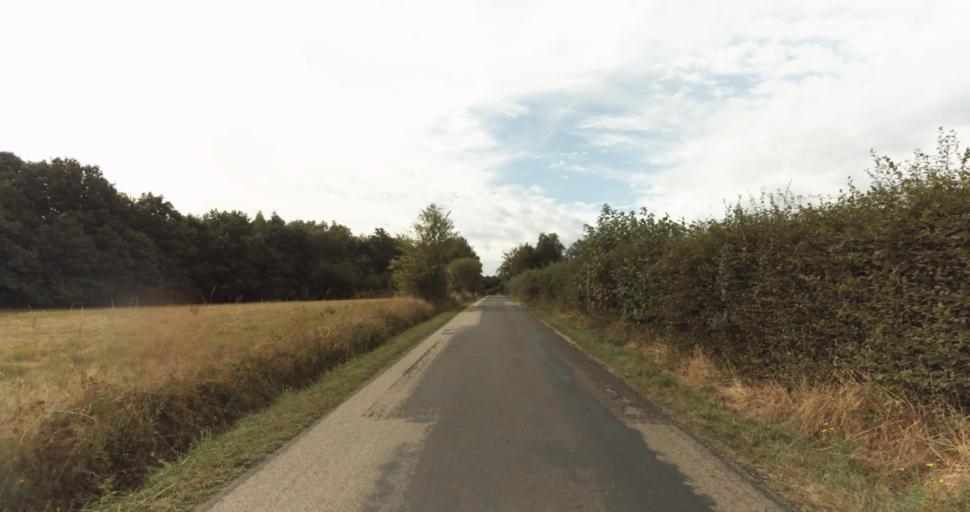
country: FR
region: Lower Normandy
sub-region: Departement de l'Orne
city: Vimoutiers
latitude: 48.9232
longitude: 0.2485
